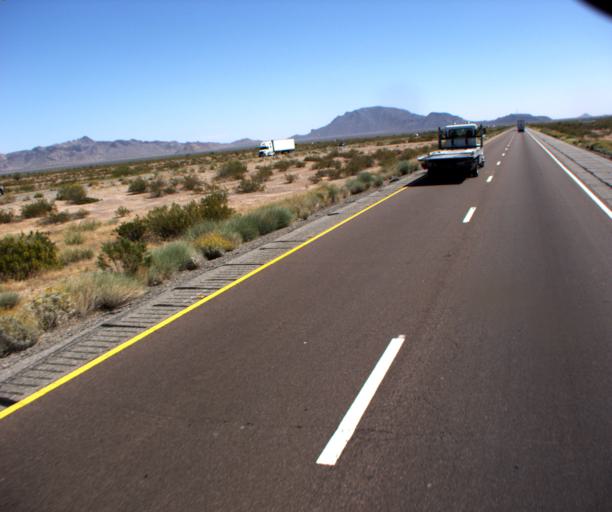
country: US
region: Arizona
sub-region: La Paz County
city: Salome
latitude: 33.5448
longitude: -113.1958
